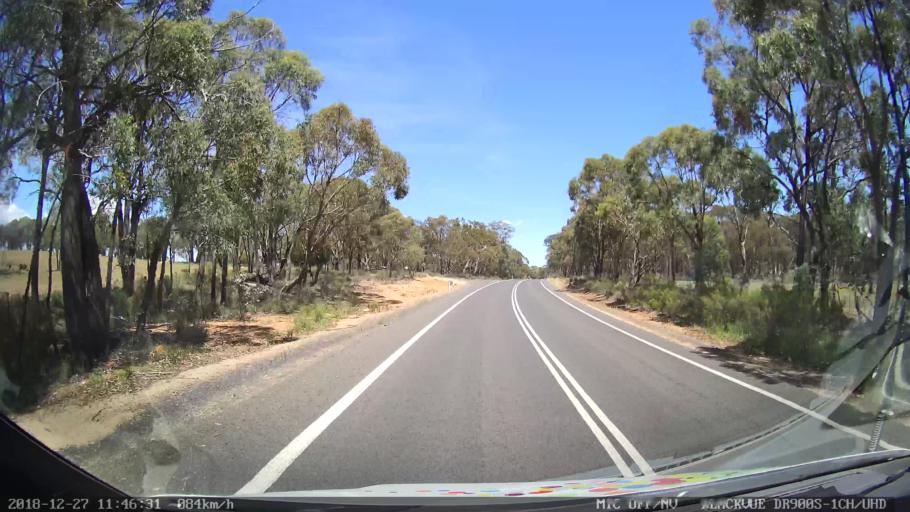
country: AU
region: New South Wales
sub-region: Bathurst Regional
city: Perthville
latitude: -33.5905
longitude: 149.4564
